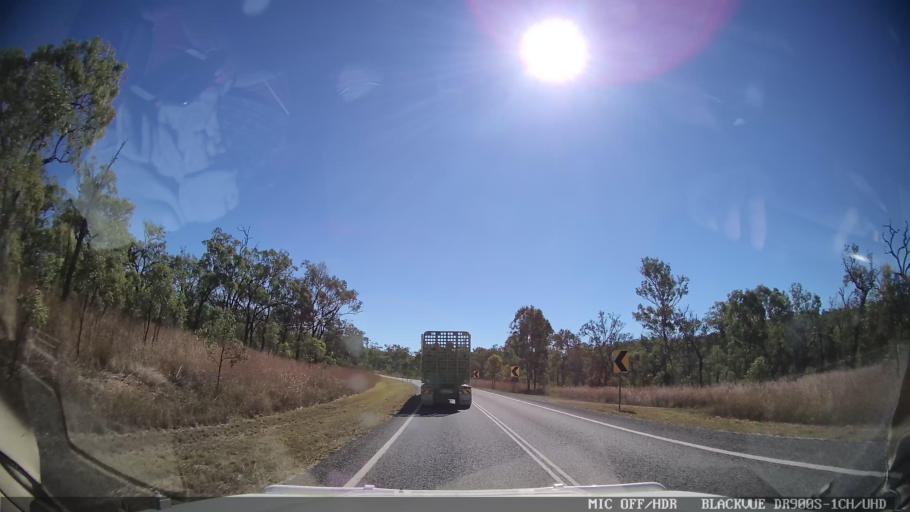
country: AU
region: Queensland
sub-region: Gladstone
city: Toolooa
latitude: -24.1509
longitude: 151.2098
